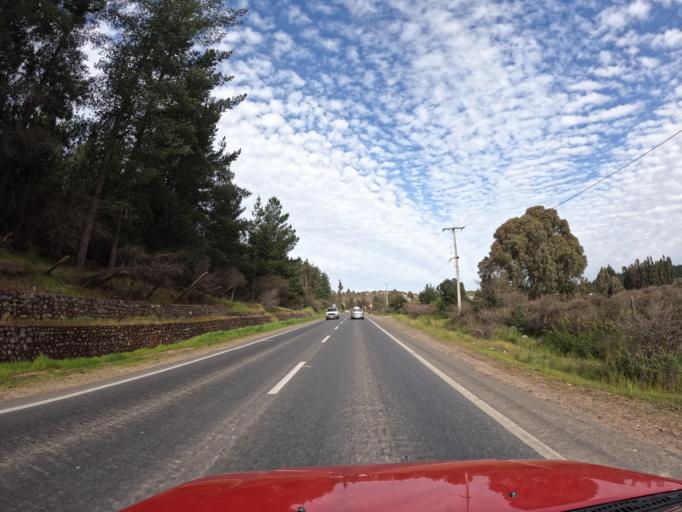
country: CL
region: O'Higgins
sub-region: Provincia de Colchagua
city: Santa Cruz
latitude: -34.3160
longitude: -71.7659
